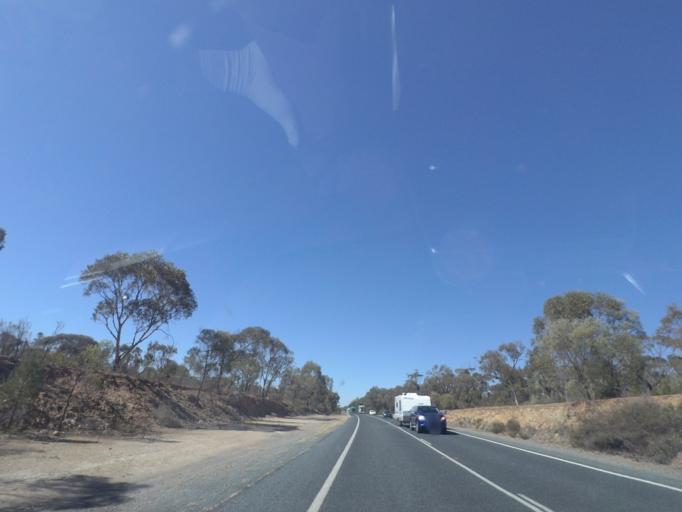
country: AU
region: New South Wales
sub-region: Bland
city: West Wyalong
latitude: -34.1387
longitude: 147.1207
